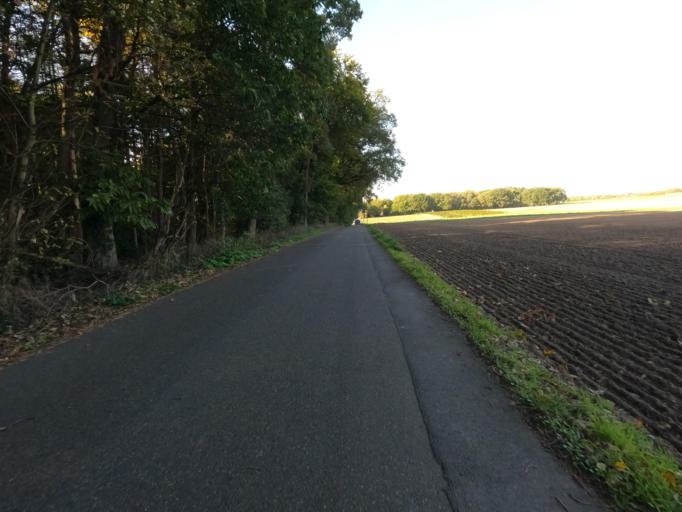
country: DE
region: North Rhine-Westphalia
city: Wegberg
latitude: 51.1297
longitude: 6.2231
